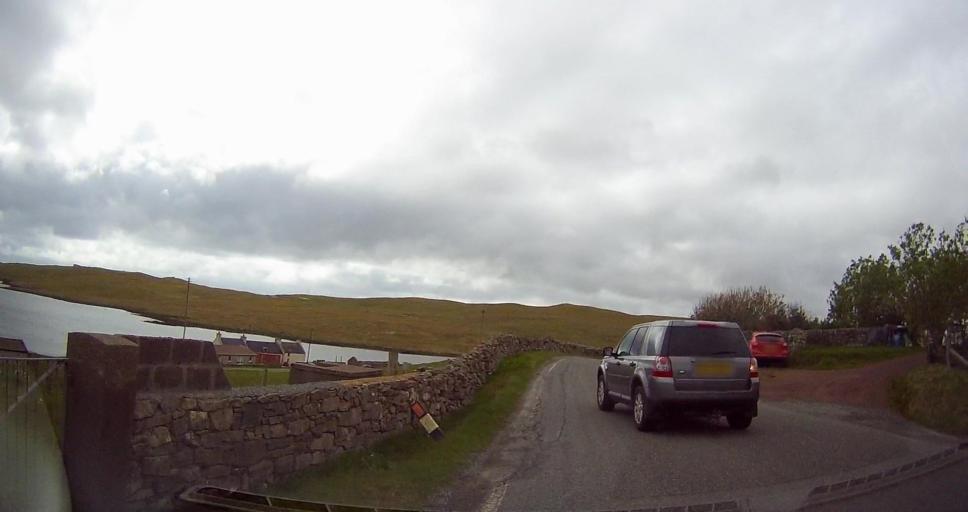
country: GB
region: Scotland
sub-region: Shetland Islands
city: Sandwick
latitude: 60.2439
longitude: -1.5225
